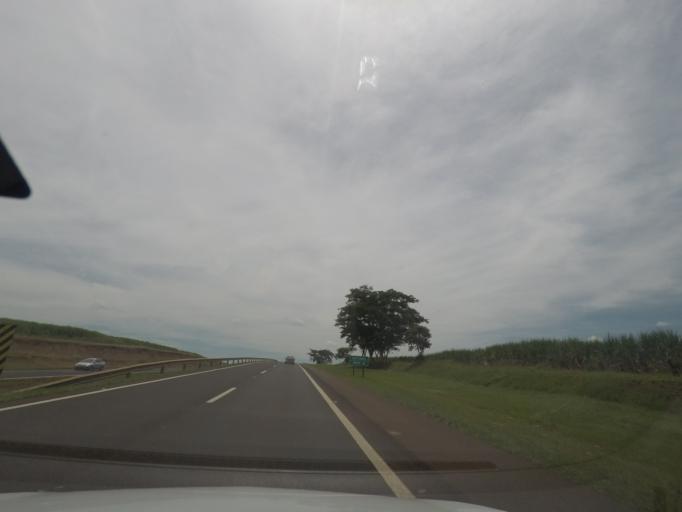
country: BR
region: Sao Paulo
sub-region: Bebedouro
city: Bebedouro
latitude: -21.0473
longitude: -48.4153
